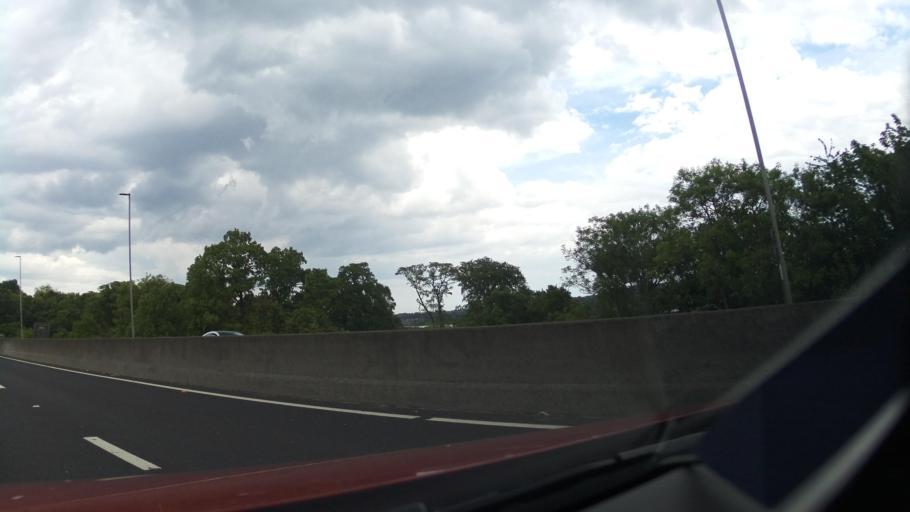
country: GB
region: England
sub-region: Gateshead
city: Lamesley
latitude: 54.9314
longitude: -1.6279
